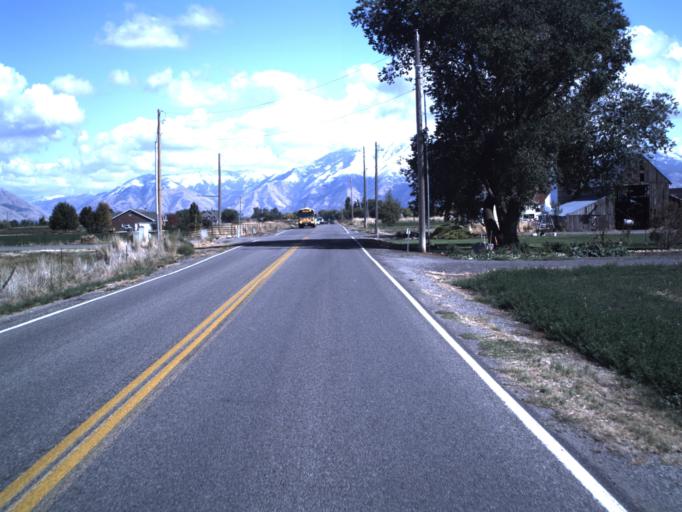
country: US
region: Utah
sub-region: Utah County
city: Benjamin
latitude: 40.1147
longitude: -111.7125
